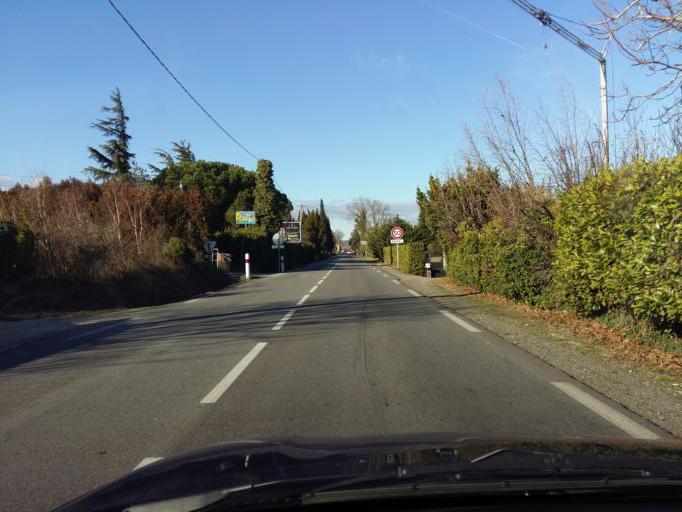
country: FR
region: Languedoc-Roussillon
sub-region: Departement du Gard
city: Pont-Saint-Esprit
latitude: 44.2694
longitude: 4.6335
